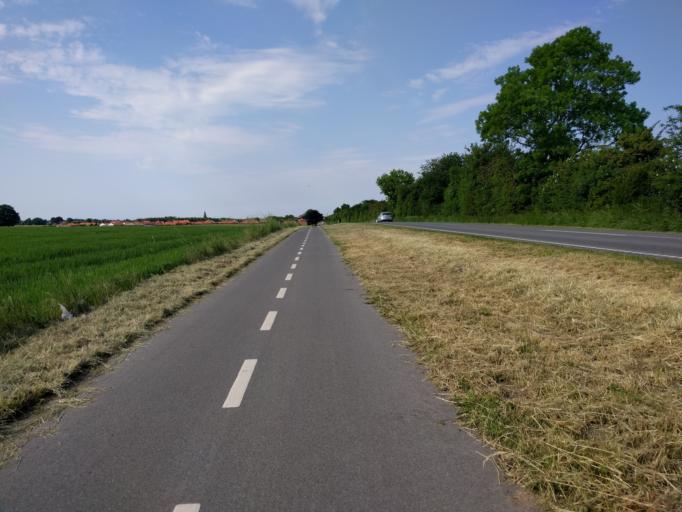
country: DK
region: South Denmark
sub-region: Kerteminde Kommune
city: Kerteminde
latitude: 55.4320
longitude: 10.6540
